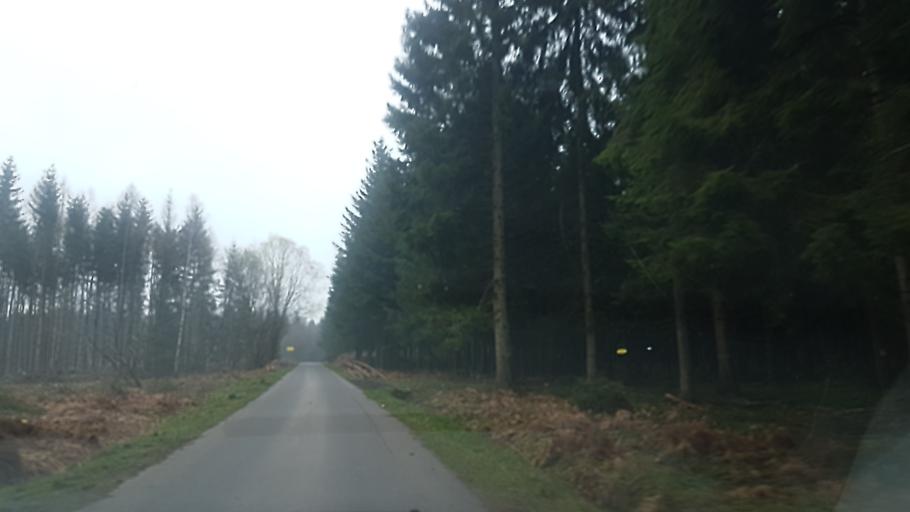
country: FR
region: Champagne-Ardenne
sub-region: Departement des Ardennes
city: Haybes
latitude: 50.0461
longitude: 4.6688
